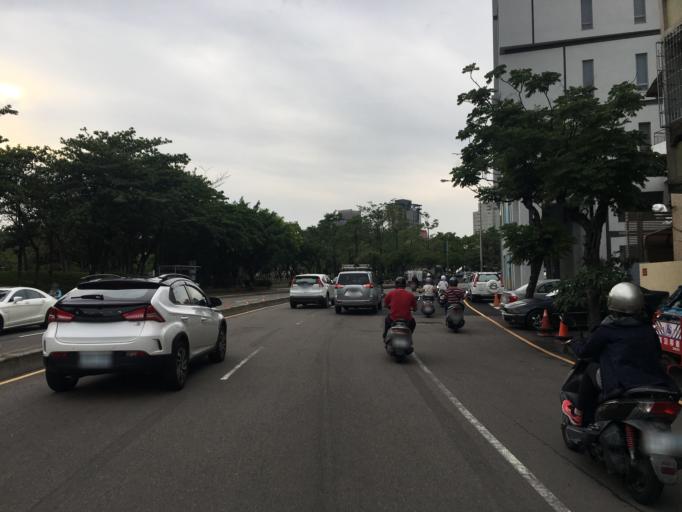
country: TW
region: Taiwan
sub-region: Taichung City
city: Taichung
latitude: 24.1419
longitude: 120.6657
